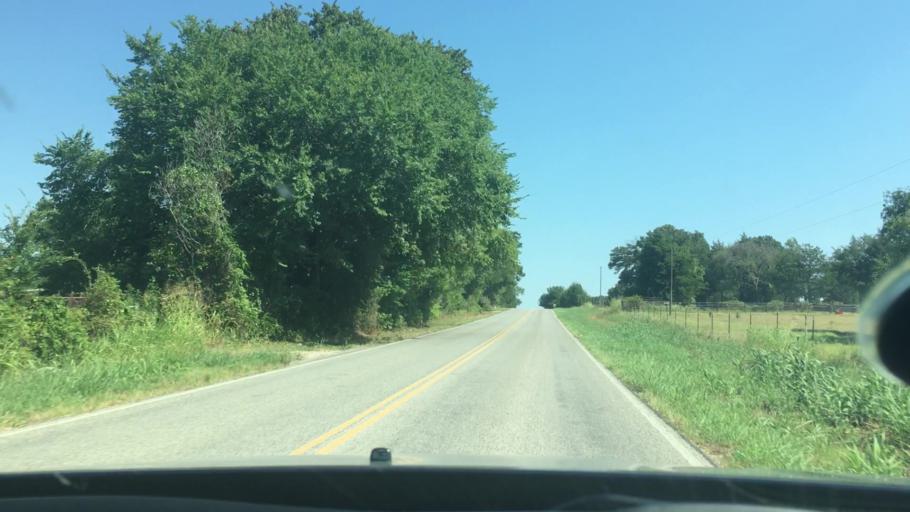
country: US
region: Oklahoma
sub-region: Johnston County
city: Tishomingo
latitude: 34.2579
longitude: -96.6186
